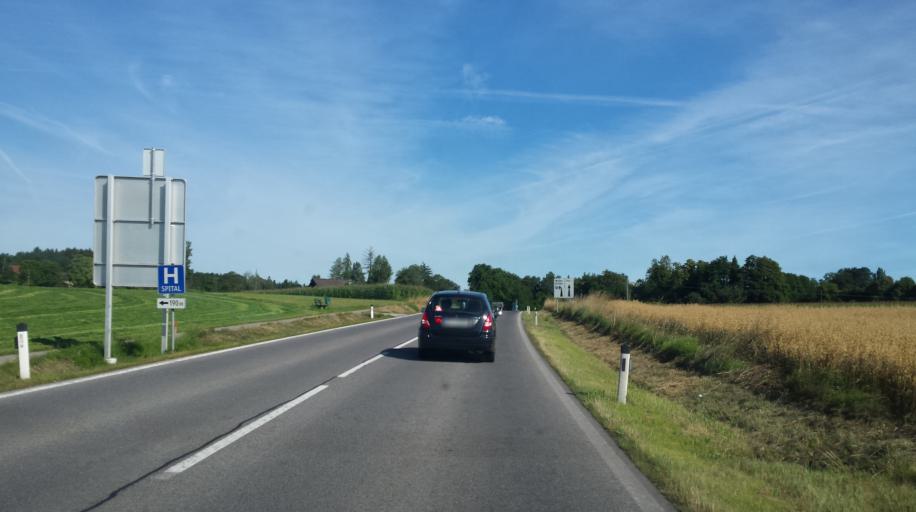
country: AT
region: Upper Austria
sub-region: Politischer Bezirk Vocklabruck
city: Sankt Georgen im Attergau
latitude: 47.9387
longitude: 13.4733
